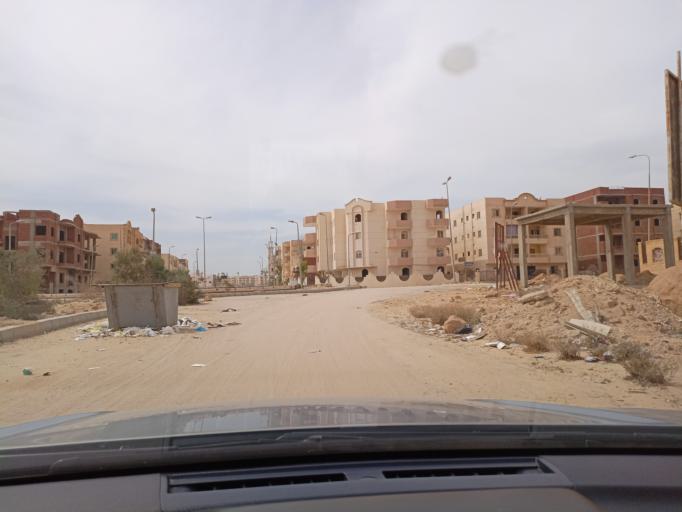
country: EG
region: Muhafazat al Qalyubiyah
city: Al Khankah
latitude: 30.2487
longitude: 31.5021
